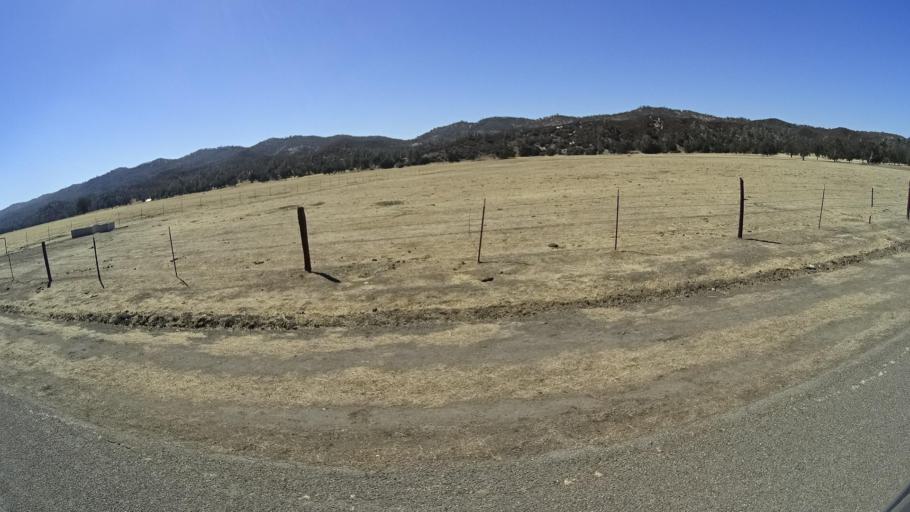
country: US
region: California
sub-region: Fresno County
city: Coalinga
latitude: 35.9577
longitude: -120.5406
